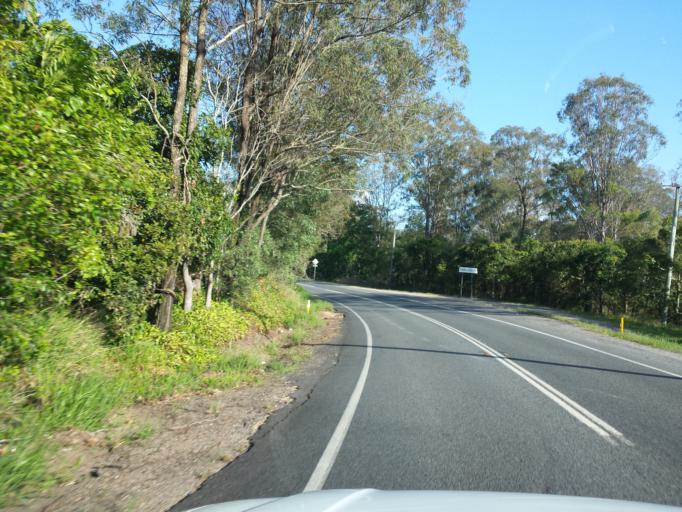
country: AU
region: Queensland
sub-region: Logan
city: Windaroo
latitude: -27.7665
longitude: 153.1907
